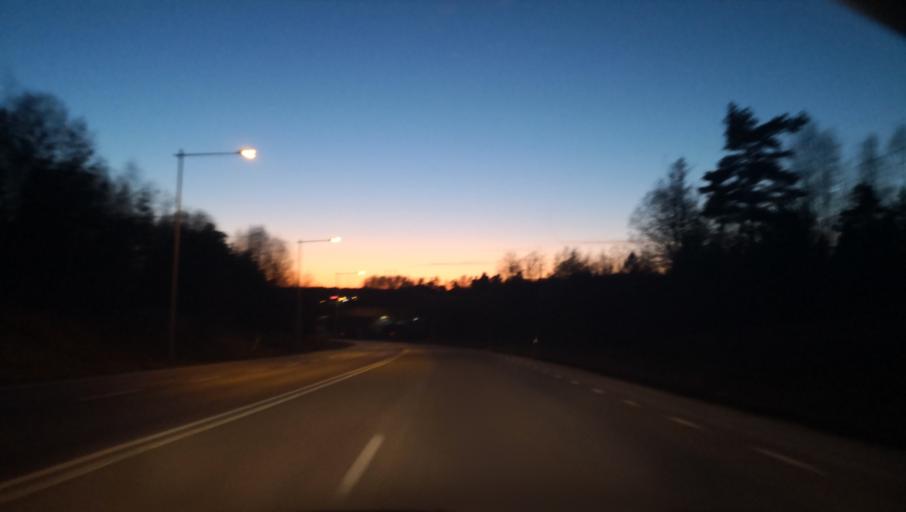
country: SE
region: Stockholm
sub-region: Nynashamns Kommun
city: Nynashamn
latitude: 58.9220
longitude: 17.9479
